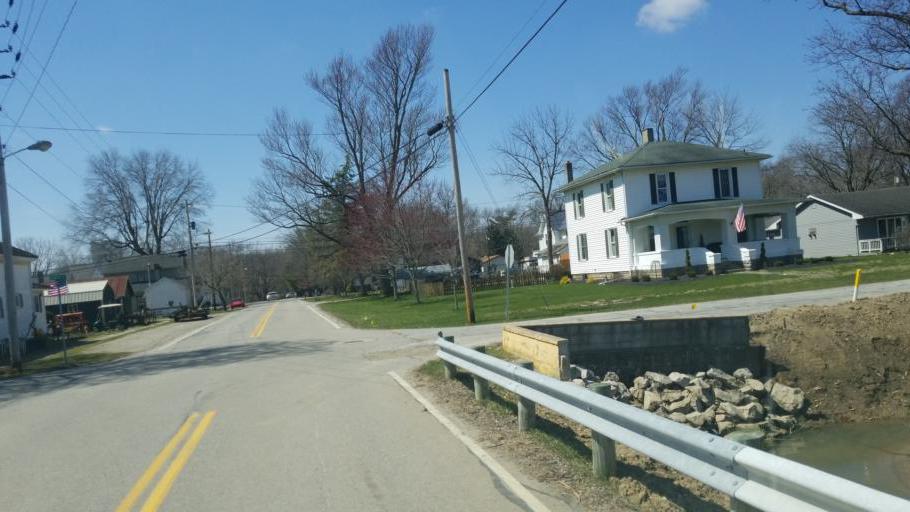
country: US
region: Ohio
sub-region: Marion County
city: Prospect
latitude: 40.4529
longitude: -83.1876
